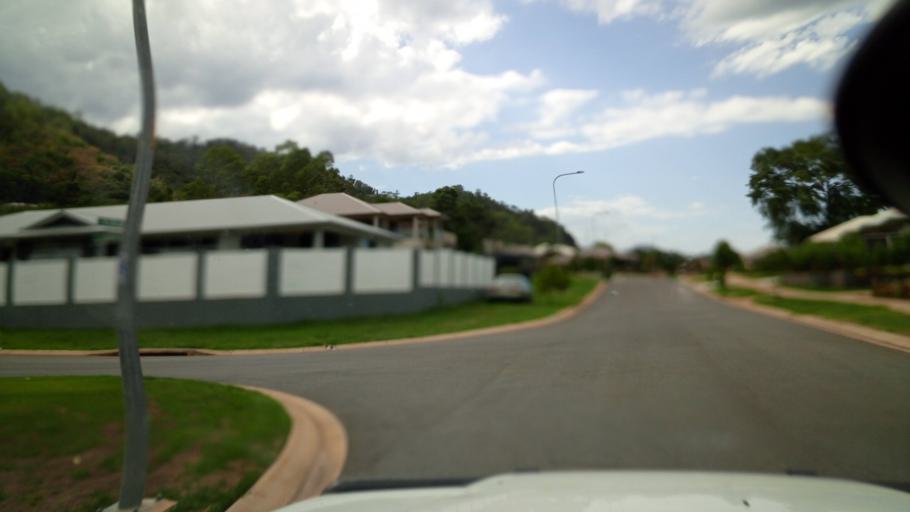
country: AU
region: Queensland
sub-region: Cairns
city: Woree
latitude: -16.9215
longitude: 145.7222
